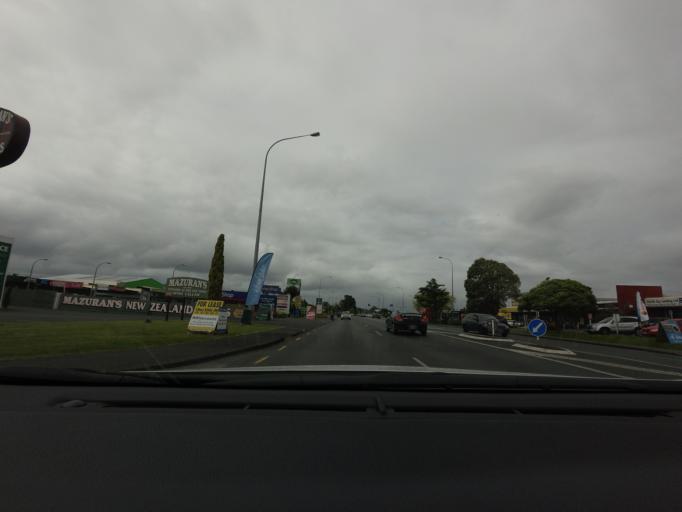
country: NZ
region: Auckland
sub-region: Auckland
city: Rosebank
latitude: -36.8556
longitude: 174.6301
